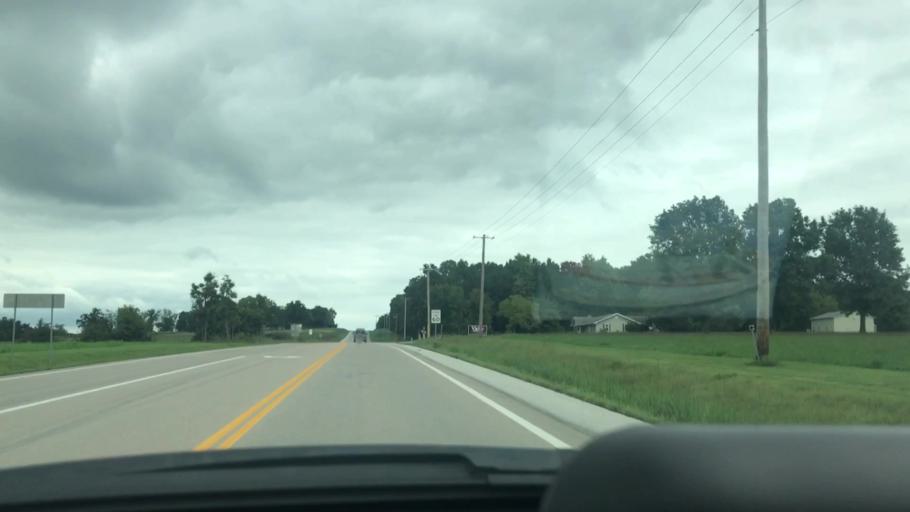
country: US
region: Missouri
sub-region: Dallas County
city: Buffalo
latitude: 37.6686
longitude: -93.1033
